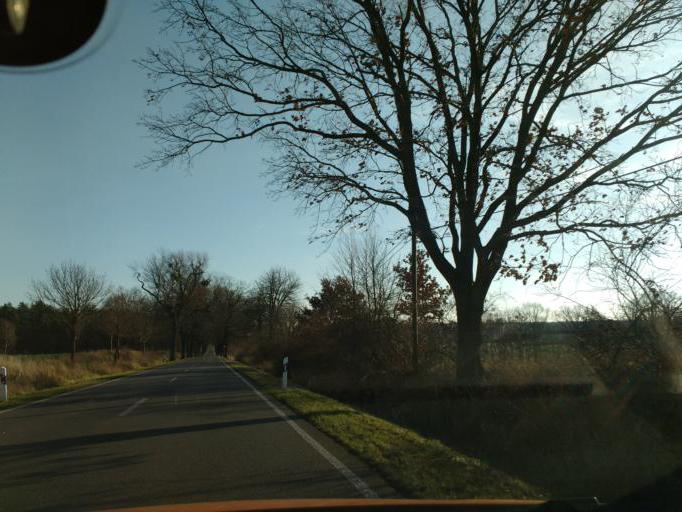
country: DE
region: Brandenburg
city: Protzel
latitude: 52.6421
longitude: 13.9708
